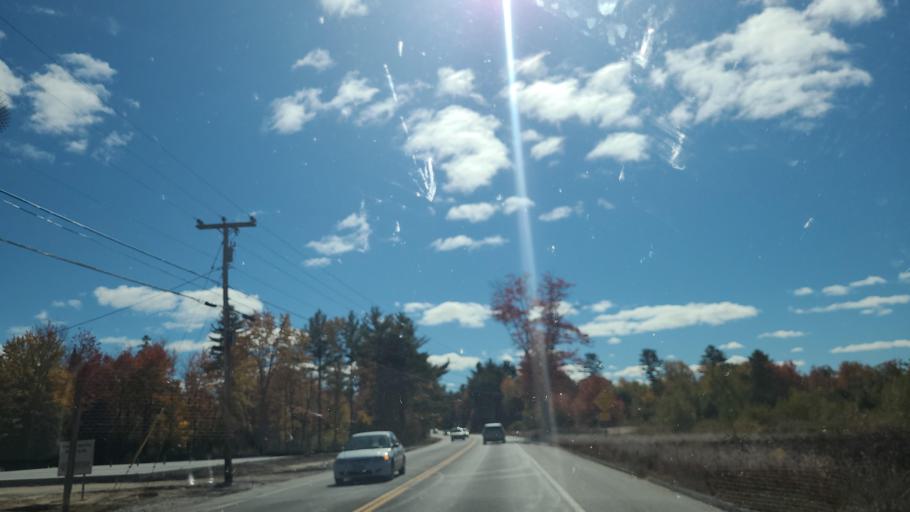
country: US
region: Maine
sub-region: Cumberland County
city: Bridgton
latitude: 44.0320
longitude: -70.6963
